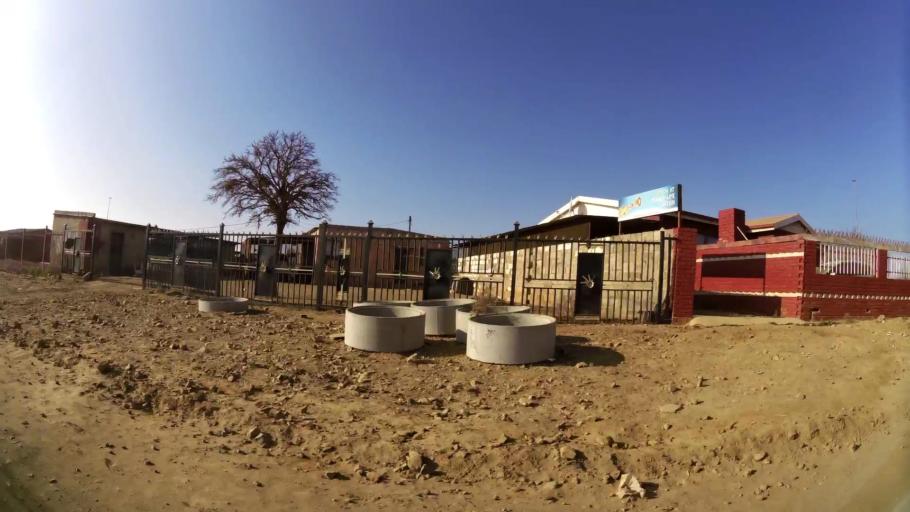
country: ZA
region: Orange Free State
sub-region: Mangaung Metropolitan Municipality
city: Bloemfontein
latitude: -29.2017
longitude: 26.2542
